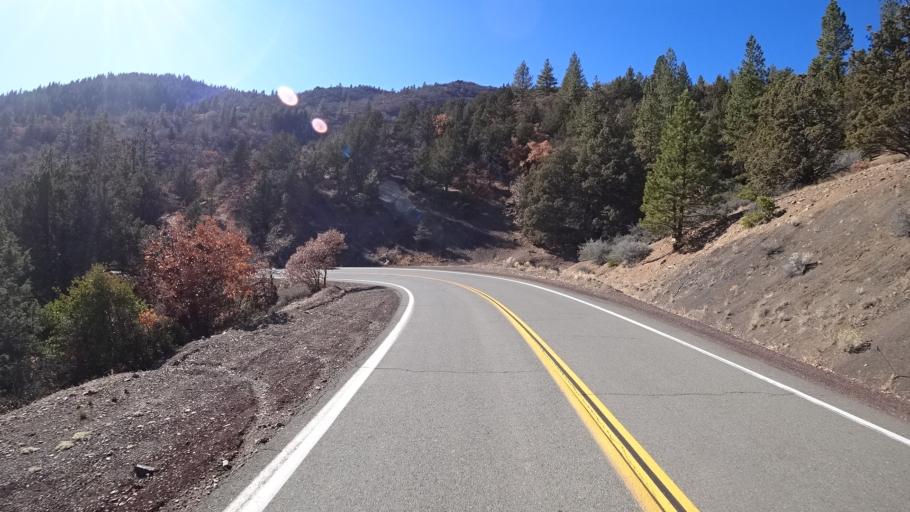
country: US
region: California
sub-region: Siskiyou County
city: Weed
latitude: 41.4501
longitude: -122.6438
